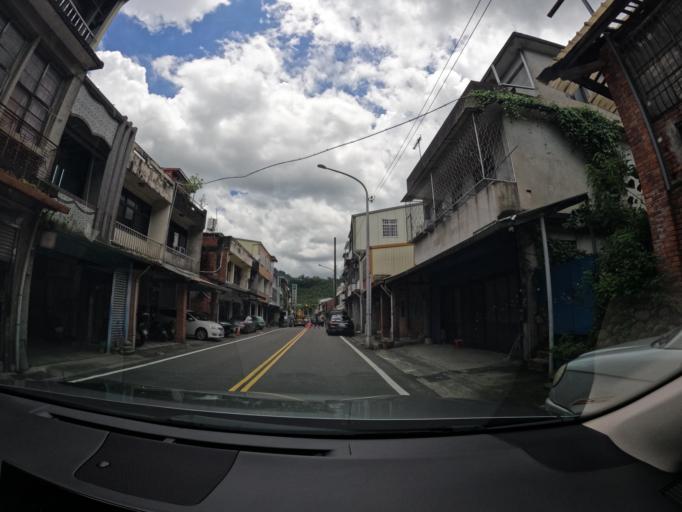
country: TW
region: Taiwan
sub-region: Hsinchu
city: Hsinchu
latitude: 24.6271
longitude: 121.0098
